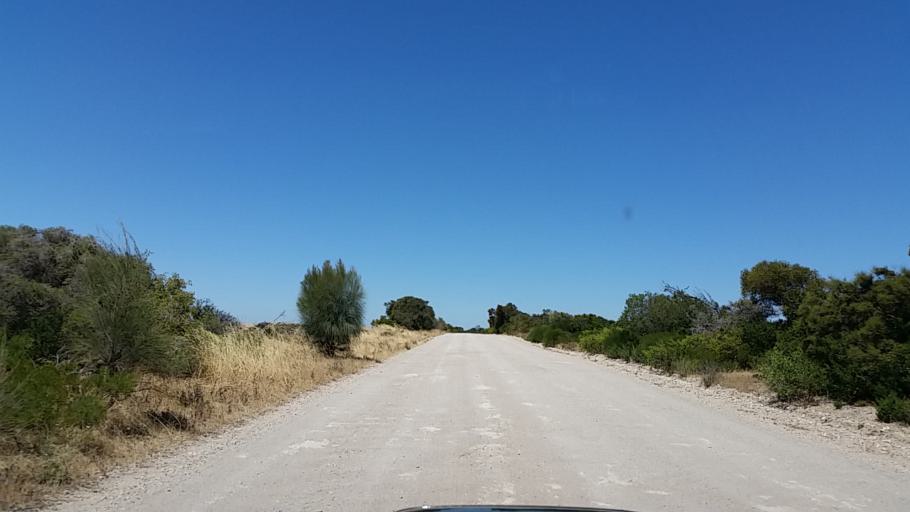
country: AU
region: South Australia
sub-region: Yorke Peninsula
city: Honiton
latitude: -35.0933
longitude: 137.4352
